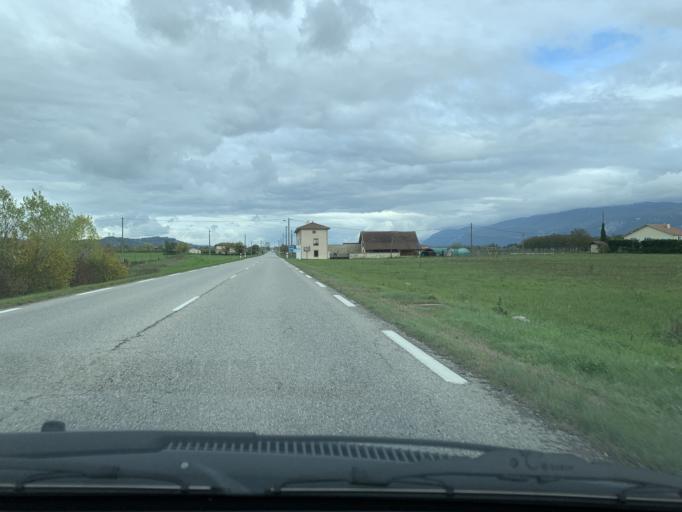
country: FR
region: Rhone-Alpes
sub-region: Departement de l'Isere
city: Saint-Hilaire-du-Rosier
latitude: 45.1116
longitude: 5.2627
